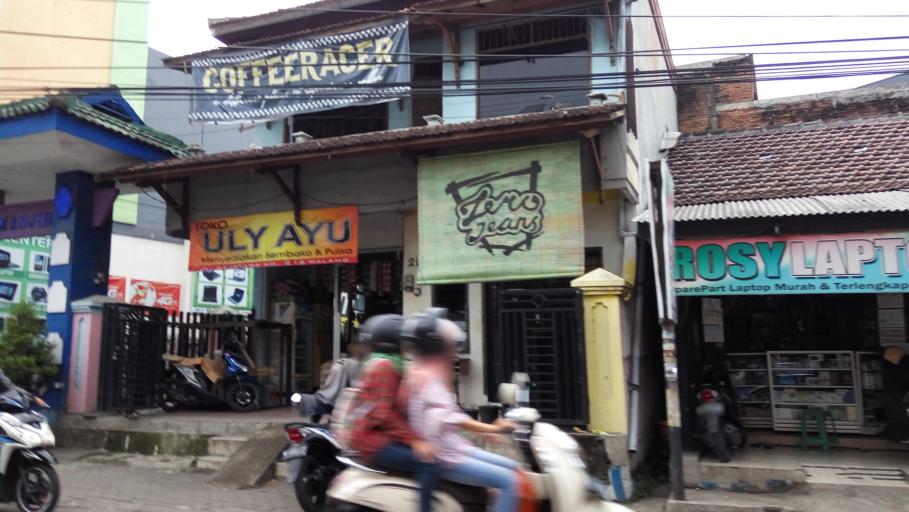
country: ID
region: East Java
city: Malang
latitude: -7.9490
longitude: 112.6089
